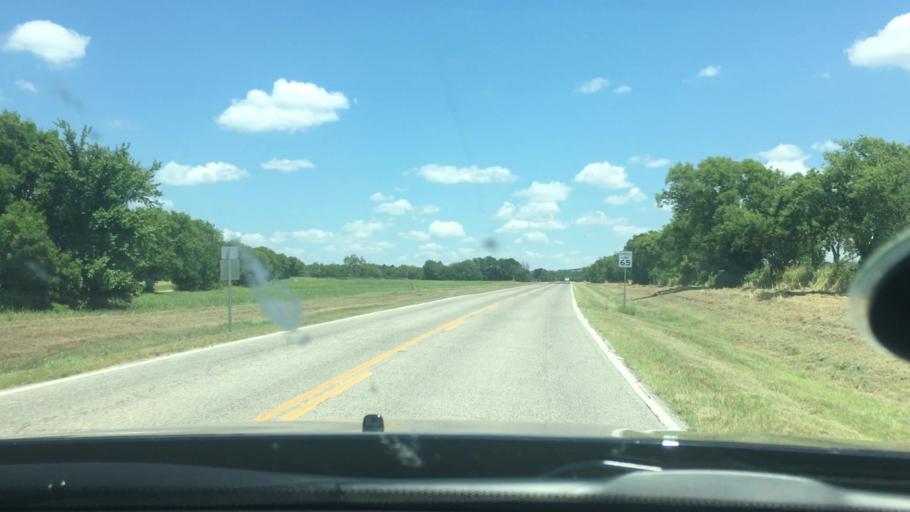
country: US
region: Oklahoma
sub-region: Carter County
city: Dickson
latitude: 34.2919
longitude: -96.9680
